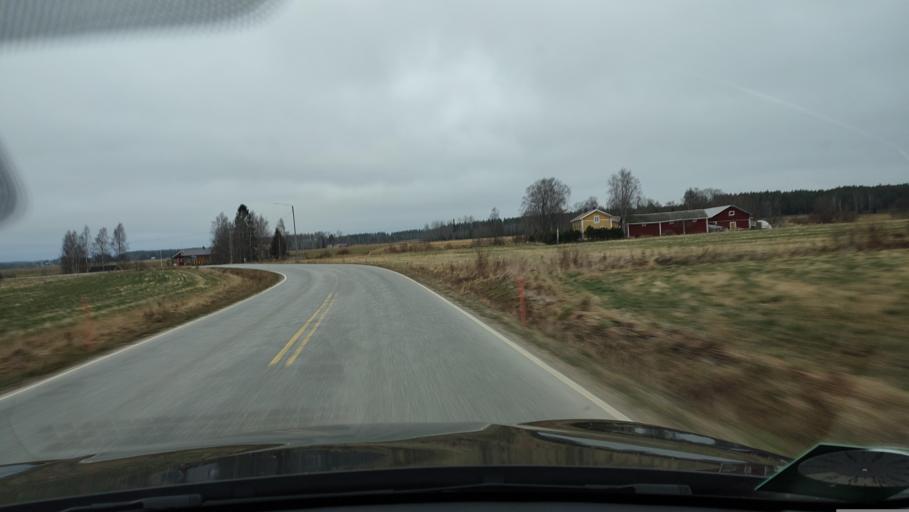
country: FI
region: Southern Ostrobothnia
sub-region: Suupohja
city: Karijoki
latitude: 62.2688
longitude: 21.7249
